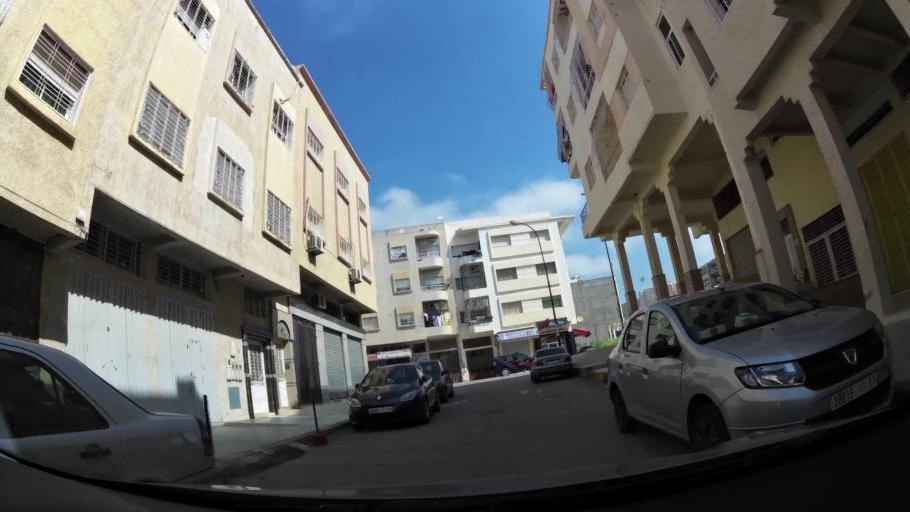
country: MA
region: Fes-Boulemane
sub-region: Fes
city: Fes
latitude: 34.0570
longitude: -5.0281
